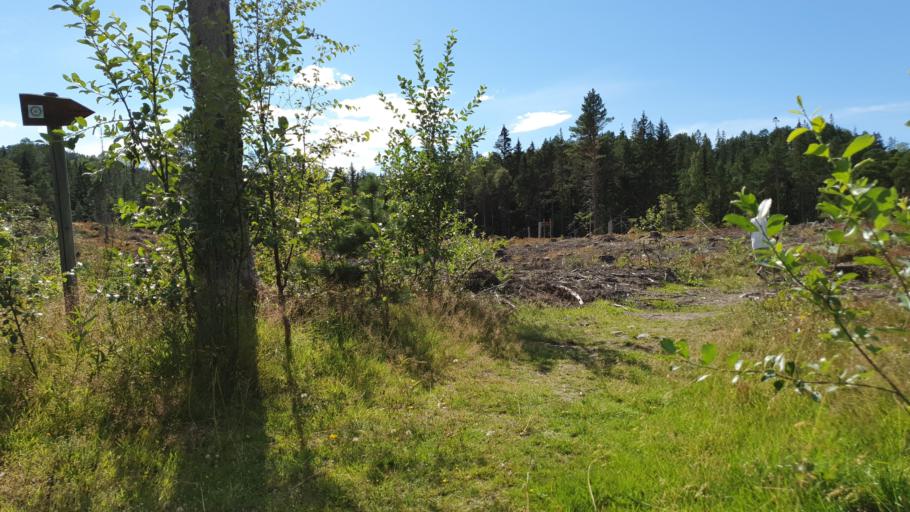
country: NO
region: Nord-Trondelag
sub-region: Levanger
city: Levanger
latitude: 63.6926
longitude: 11.2753
